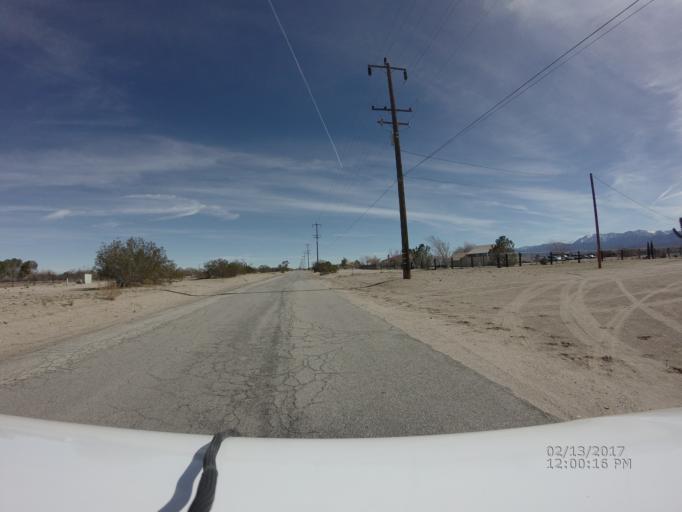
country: US
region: California
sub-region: Los Angeles County
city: Littlerock
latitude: 34.5579
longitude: -117.9311
